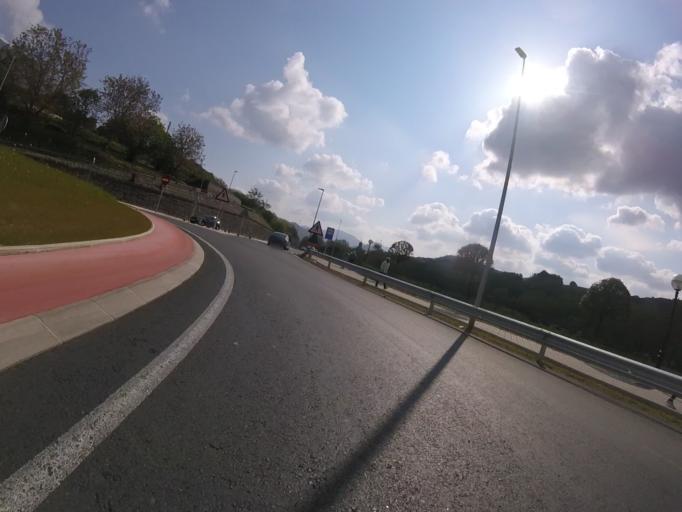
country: ES
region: Basque Country
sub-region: Provincia de Guipuzcoa
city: Azkoitia
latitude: 43.1742
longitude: -2.2914
